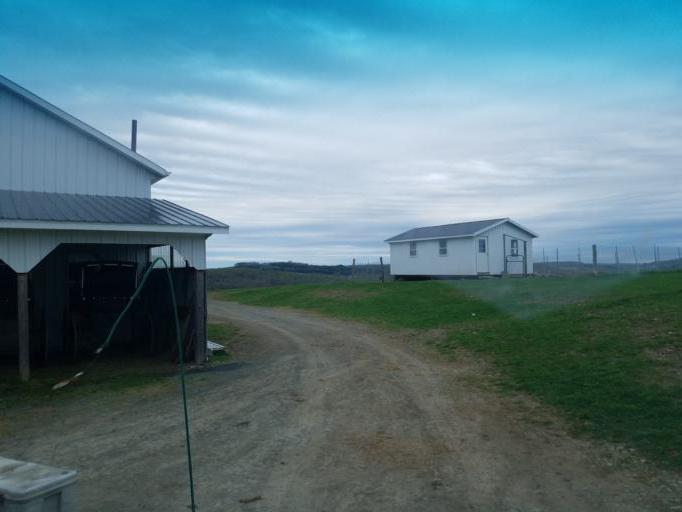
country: US
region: New York
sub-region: Allegany County
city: Andover
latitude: 42.0219
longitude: -77.7593
